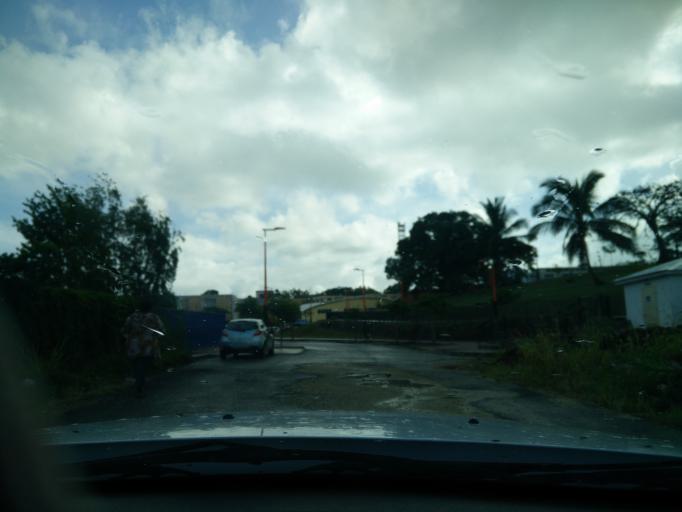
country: GP
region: Guadeloupe
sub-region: Guadeloupe
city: Pointe-a-Pitre
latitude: 16.2513
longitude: -61.5346
